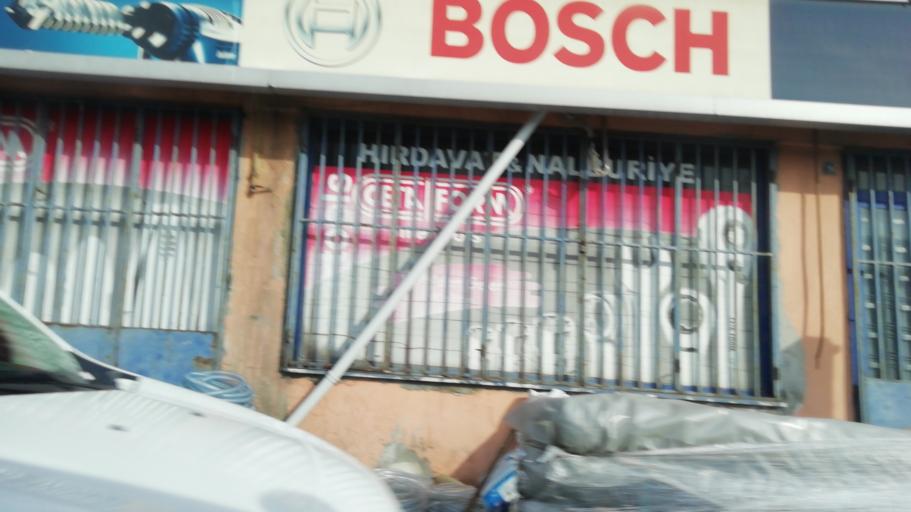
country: TR
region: Istanbul
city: Basaksehir
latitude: 41.0955
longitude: 28.7936
